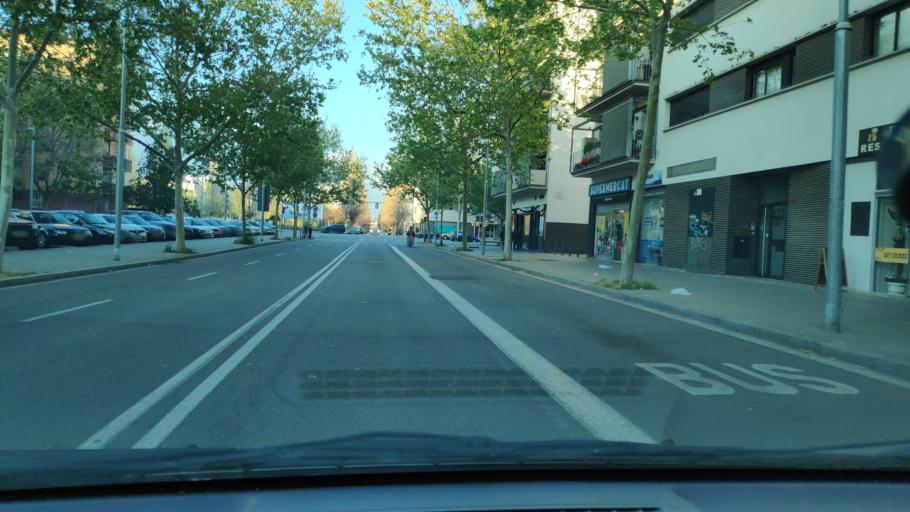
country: ES
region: Catalonia
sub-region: Provincia de Barcelona
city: Sant Adria de Besos
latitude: 41.4139
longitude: 2.2194
